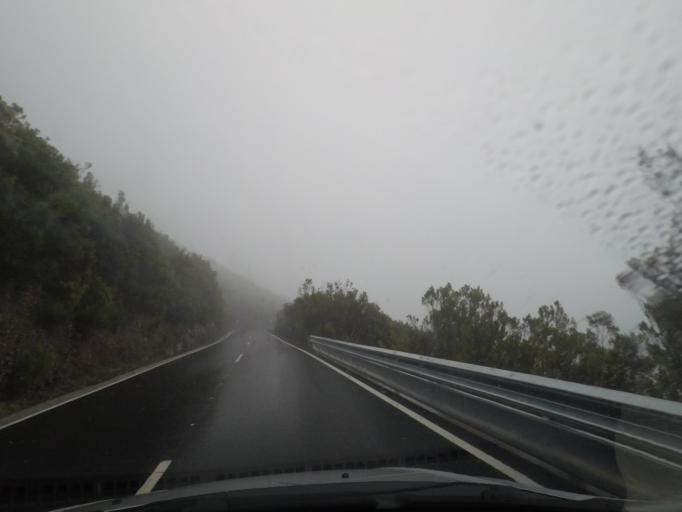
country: PT
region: Madeira
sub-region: Santana
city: Santana
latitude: 32.7674
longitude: -16.9204
